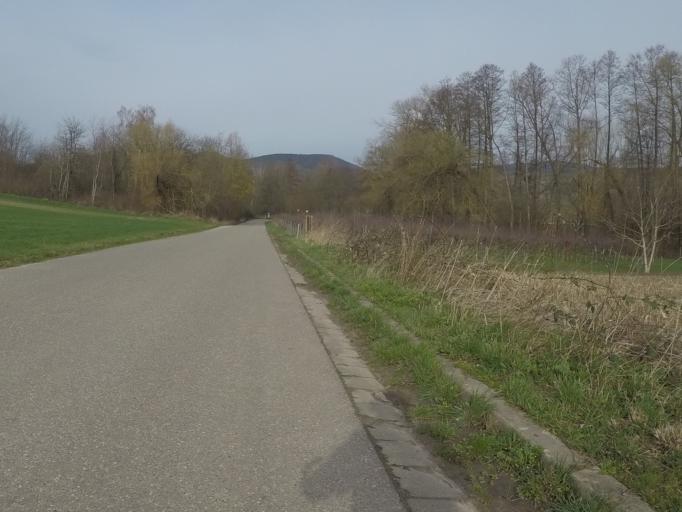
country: DE
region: Rheinland-Pfalz
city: Heuchelheim-Klingen
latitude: 49.1393
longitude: 8.0397
